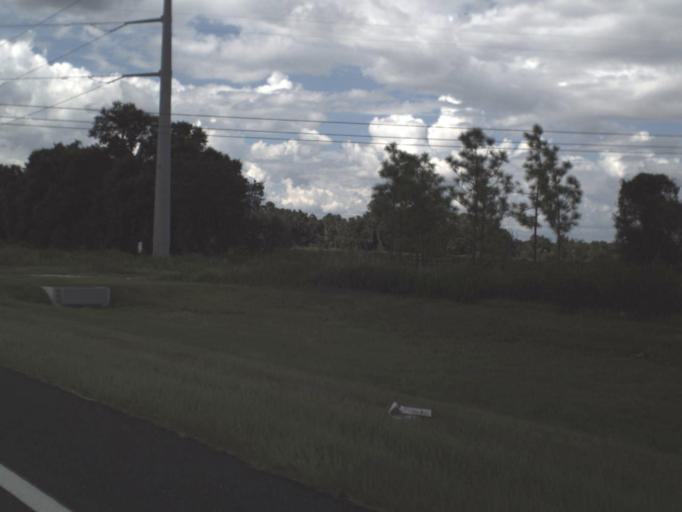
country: US
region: Florida
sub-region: Polk County
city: Bartow
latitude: 27.9309
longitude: -81.8550
